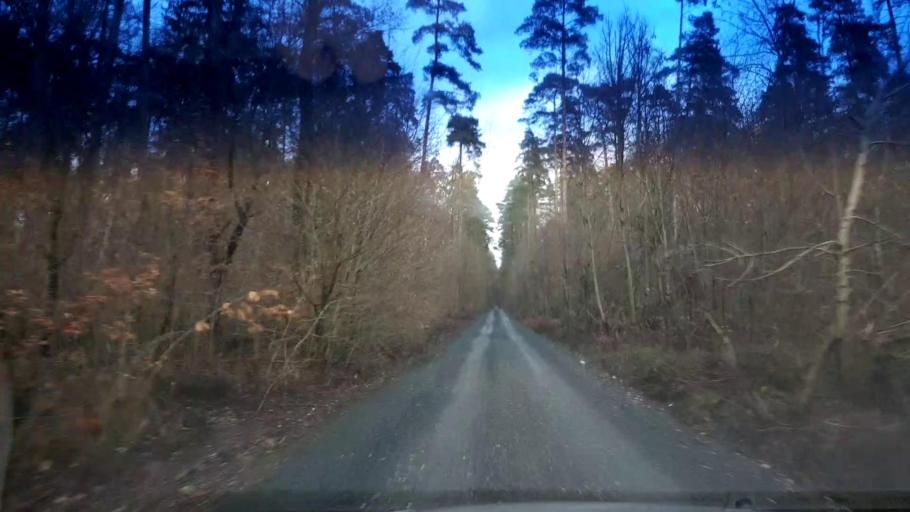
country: DE
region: Bavaria
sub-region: Regierungsbezirk Unterfranken
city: Stettfeld
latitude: 49.9740
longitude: 10.7413
